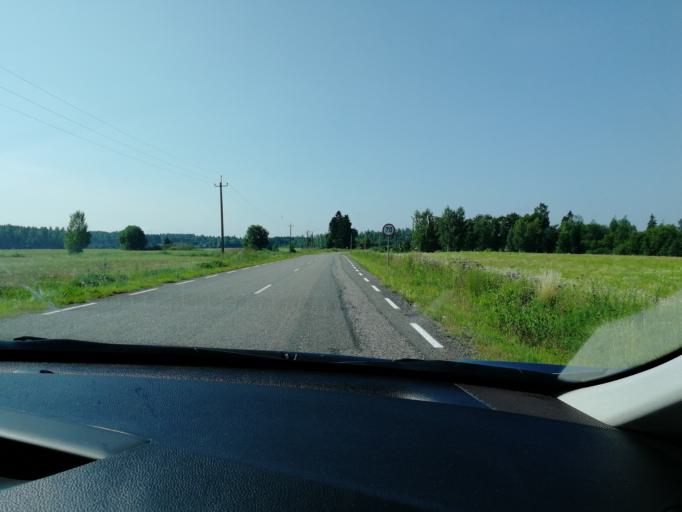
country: EE
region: Paernumaa
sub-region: Saarde vald
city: Kilingi-Nomme
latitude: 58.0237
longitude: 25.0094
